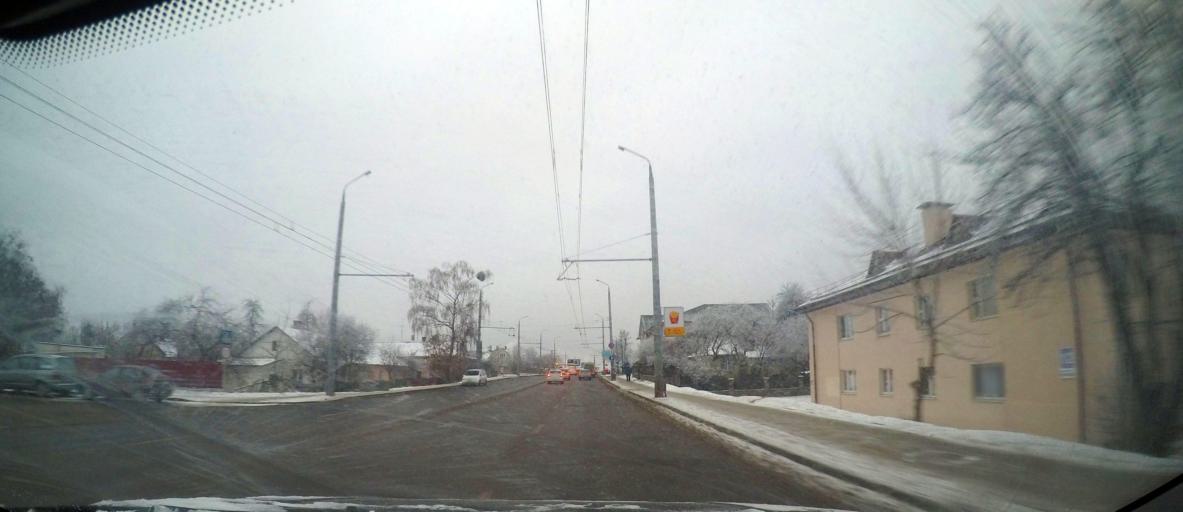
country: BY
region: Grodnenskaya
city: Hrodna
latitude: 53.6607
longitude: 23.8334
